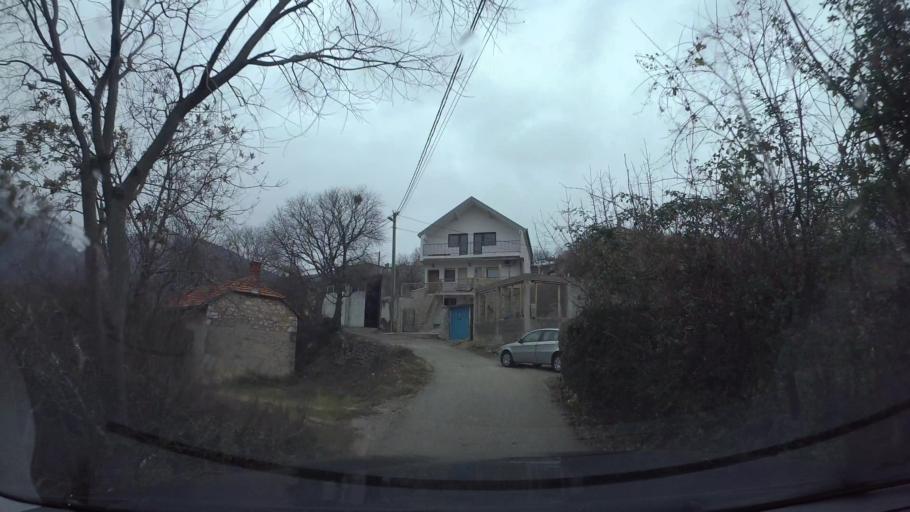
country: BA
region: Federation of Bosnia and Herzegovina
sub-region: Hercegovacko-Bosanski Kanton
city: Mostar
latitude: 43.3603
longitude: 17.8172
